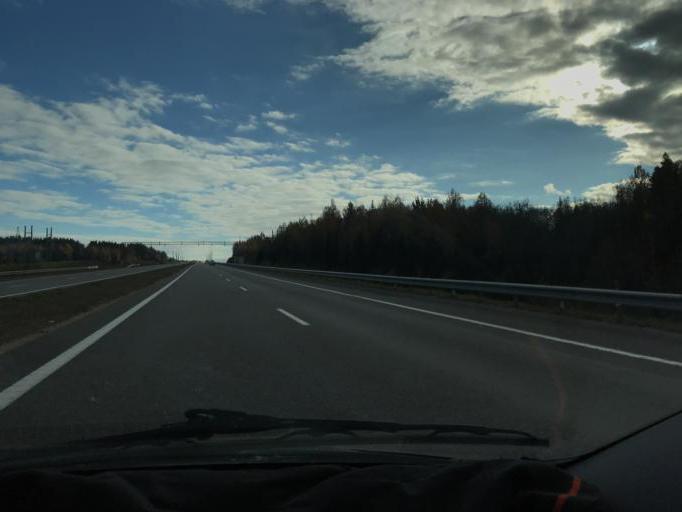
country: BY
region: Minsk
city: Lahoysk
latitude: 54.1857
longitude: 27.8168
